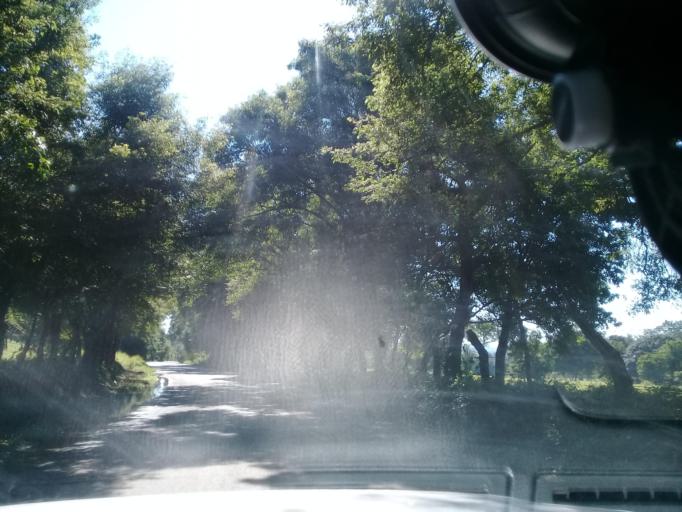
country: MX
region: Hidalgo
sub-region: Huejutla de Reyes
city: Huejutla de Reyes
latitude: 21.1664
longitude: -98.4211
